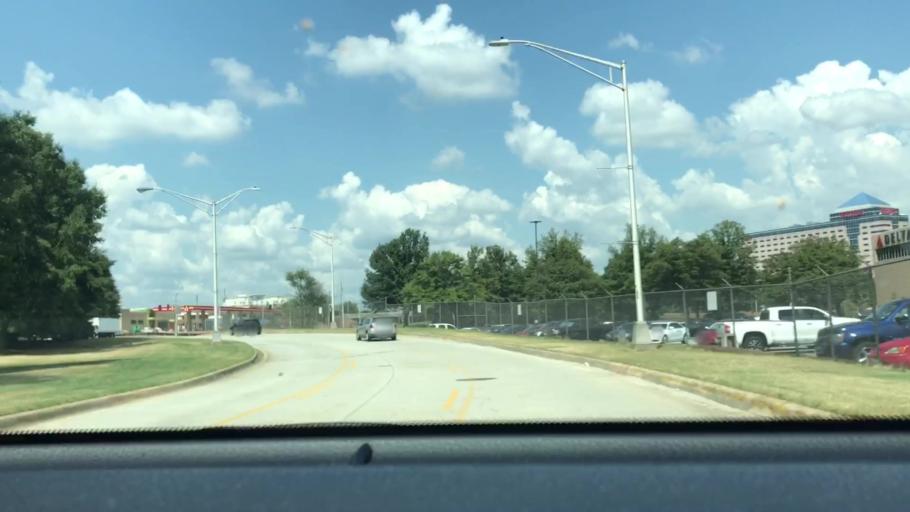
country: US
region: Georgia
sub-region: Fulton County
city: Hapeville
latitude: 33.6560
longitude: -84.4260
